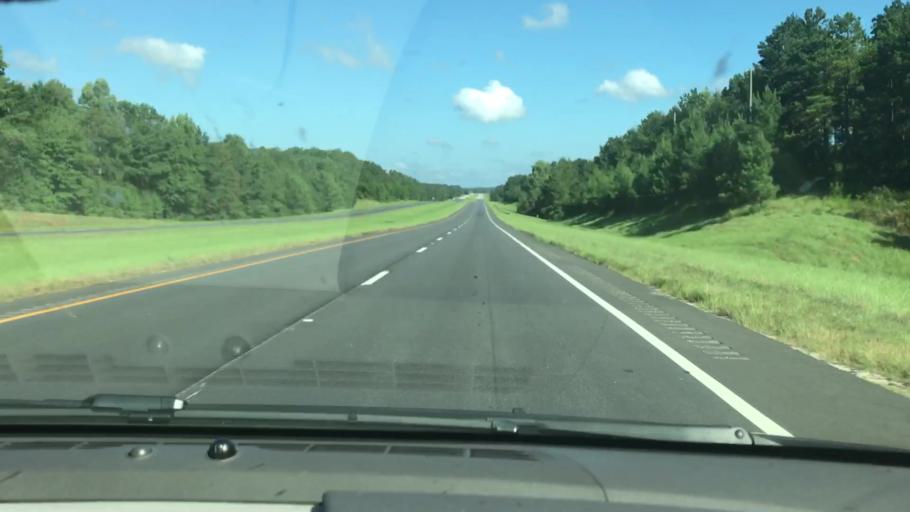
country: US
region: Alabama
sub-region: Barbour County
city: Eufaula
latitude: 32.0526
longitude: -85.1345
